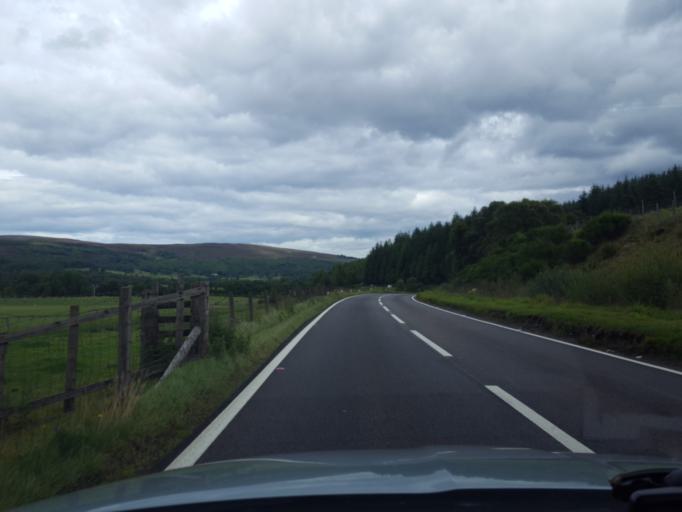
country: GB
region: Scotland
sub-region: Highland
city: Grantown on Spey
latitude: 57.3481
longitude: -3.5266
